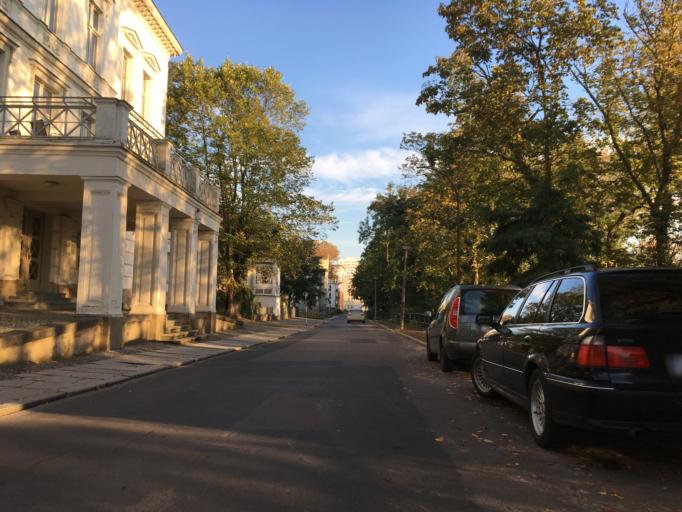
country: DE
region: Brandenburg
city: Frankfurt (Oder)
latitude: 52.3439
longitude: 14.5479
